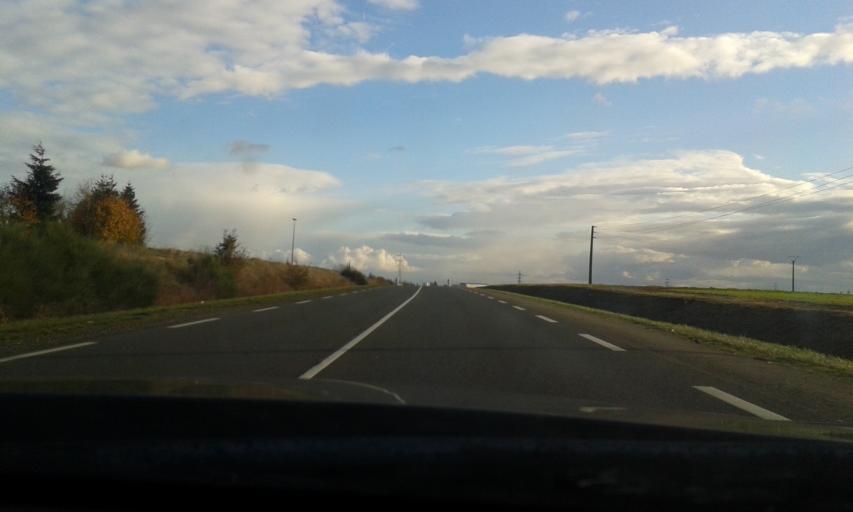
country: FR
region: Centre
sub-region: Departement d'Eure-et-Loir
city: Leves
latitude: 48.4741
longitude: 1.4620
